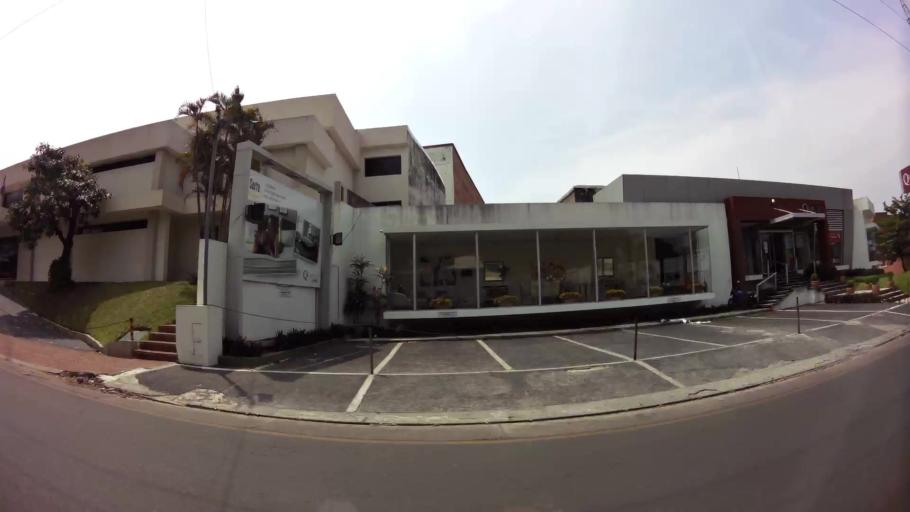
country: PY
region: Asuncion
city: Asuncion
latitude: -25.2877
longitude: -57.5994
